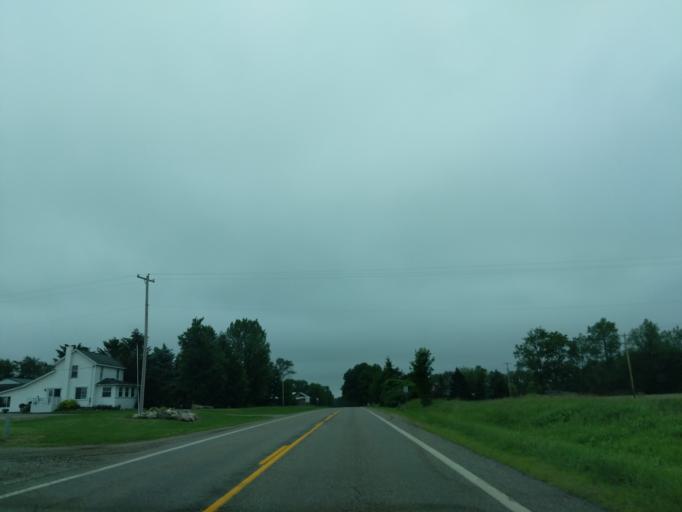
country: US
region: Michigan
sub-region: Calhoun County
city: Homer
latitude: 42.0850
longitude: -84.8029
